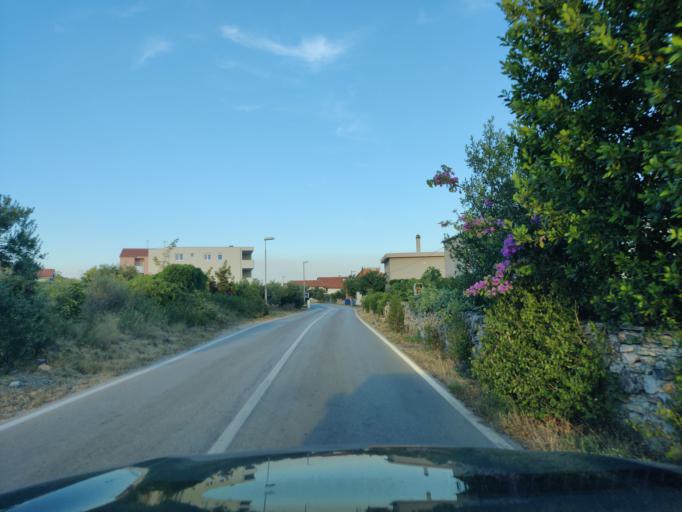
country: HR
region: Sibensko-Kniniska
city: Tribunj
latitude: 43.7596
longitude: 15.7496
